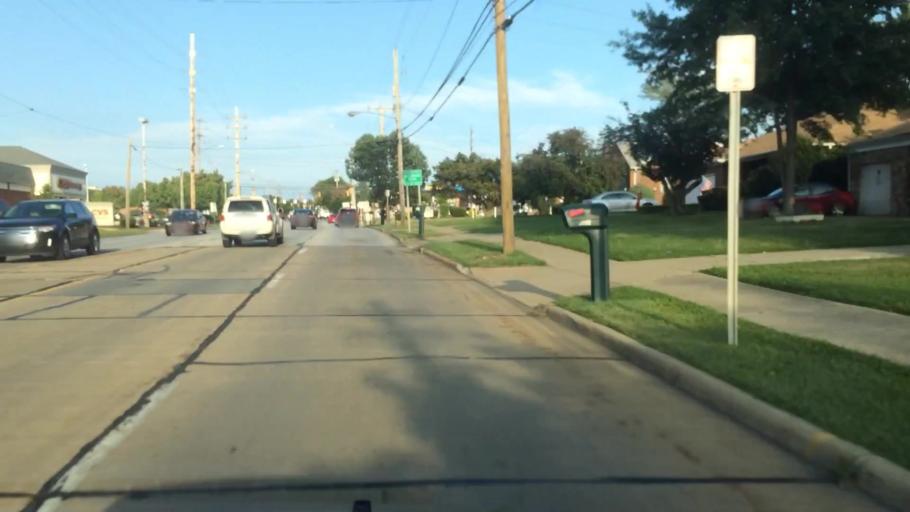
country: US
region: Ohio
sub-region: Cuyahoga County
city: Richmond Heights
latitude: 41.5388
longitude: -81.5007
